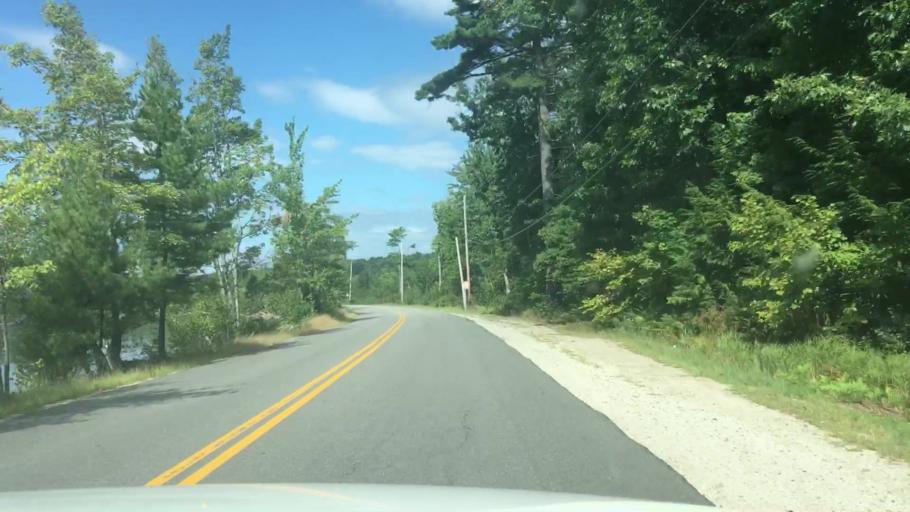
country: US
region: Maine
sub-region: Androscoggin County
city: Auburn
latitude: 44.1579
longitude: -70.2383
